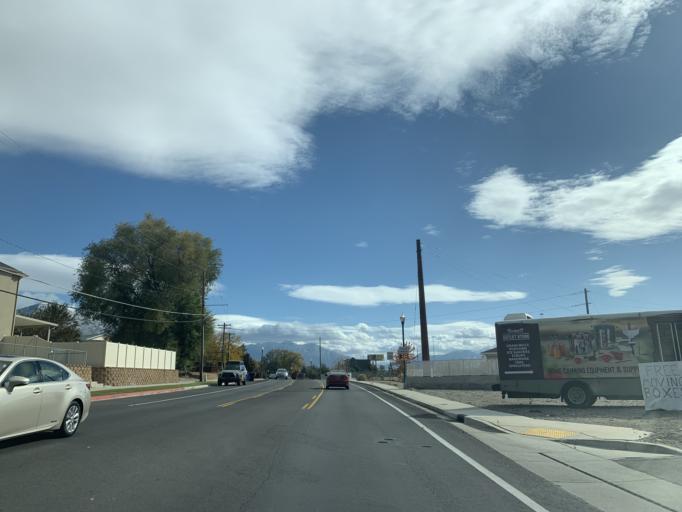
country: US
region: Utah
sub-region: Utah County
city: Orem
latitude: 40.2644
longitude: -111.7074
